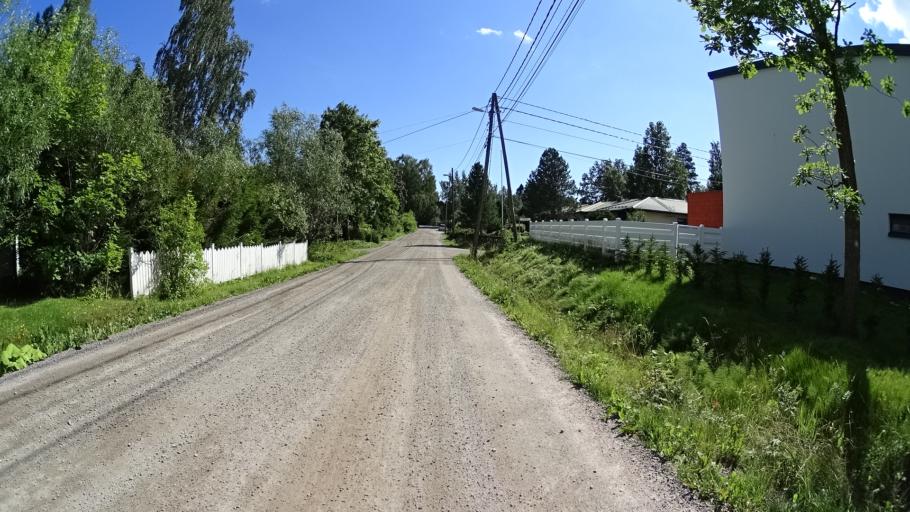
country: FI
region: Uusimaa
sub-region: Helsinki
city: Kauniainen
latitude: 60.2287
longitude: 24.7074
